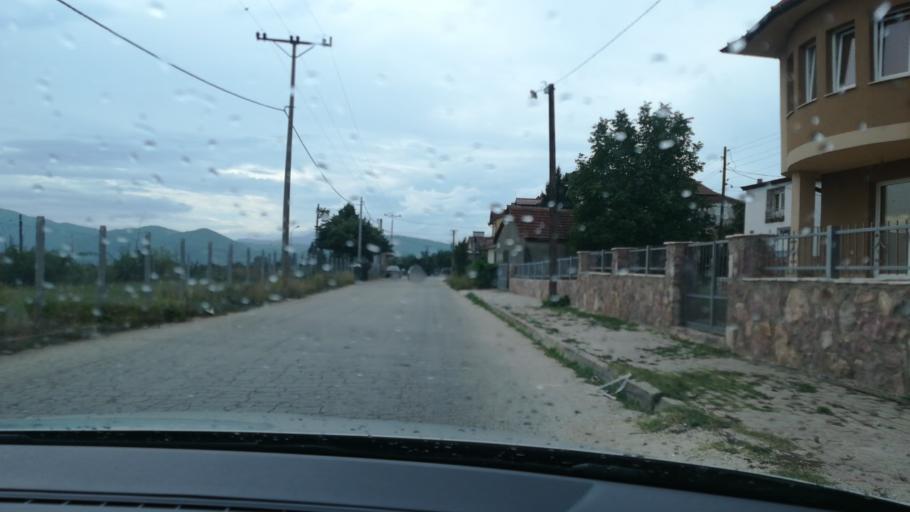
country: MK
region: Kicevo
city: Kicevo
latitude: 41.5169
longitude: 20.9504
